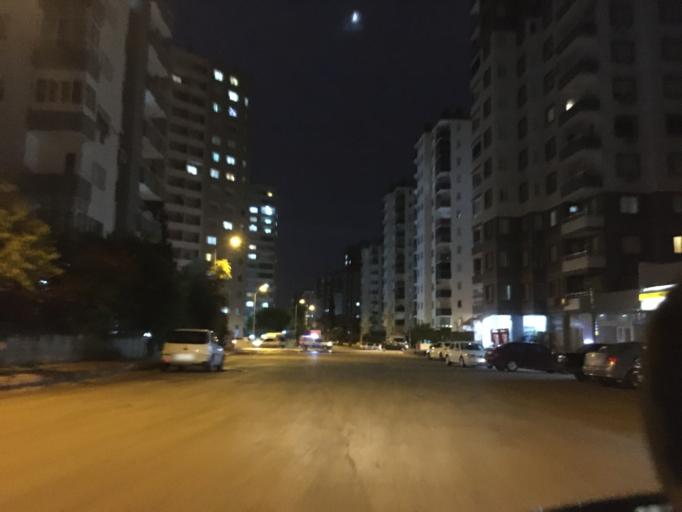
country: TR
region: Adana
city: Seyhan
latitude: 37.0277
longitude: 35.2834
